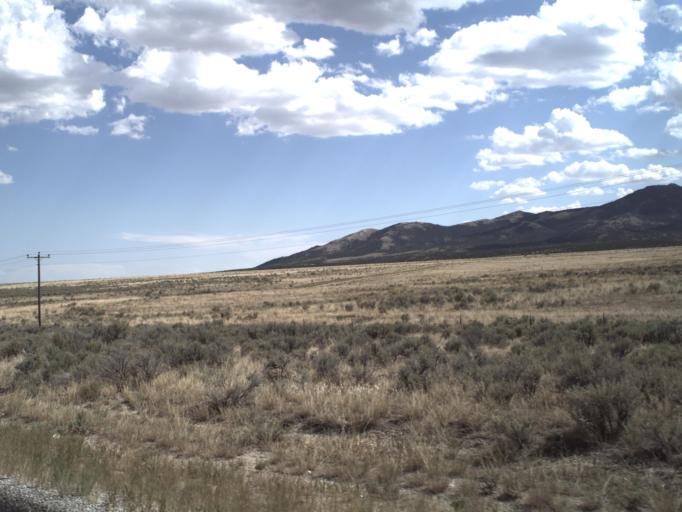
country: US
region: Idaho
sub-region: Minidoka County
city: Rupert
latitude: 41.9911
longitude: -113.1848
